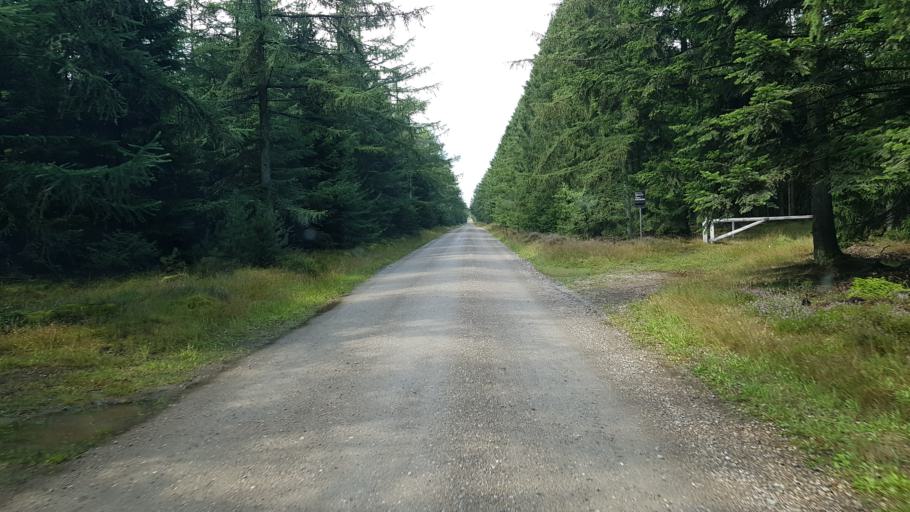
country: DK
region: South Denmark
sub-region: Vejen Kommune
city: Holsted
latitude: 55.5953
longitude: 8.8997
